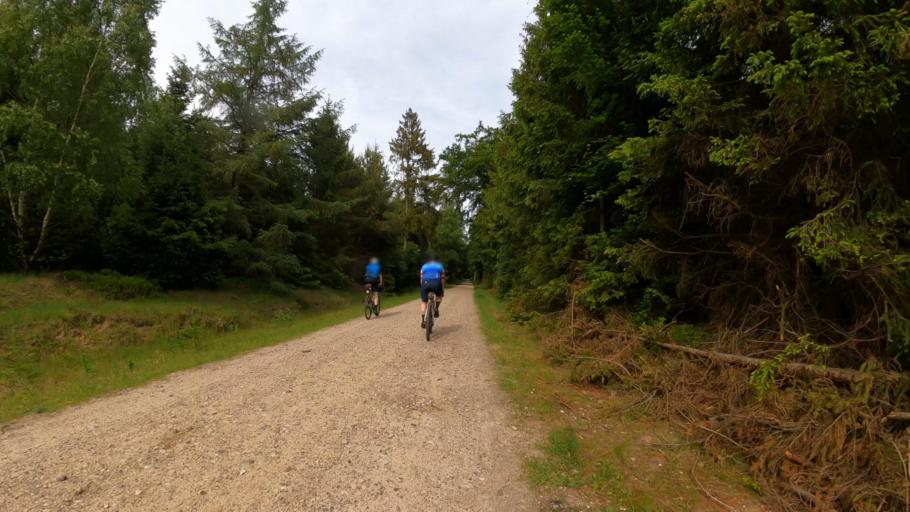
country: DE
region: Schleswig-Holstein
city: Heidmuhlen
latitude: 53.9479
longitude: 10.1109
